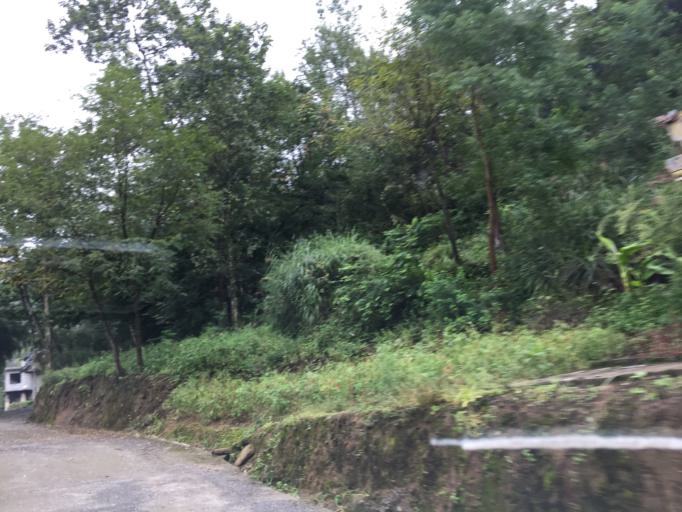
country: CN
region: Guizhou Sheng
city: Longquan
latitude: 28.2102
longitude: 108.0555
